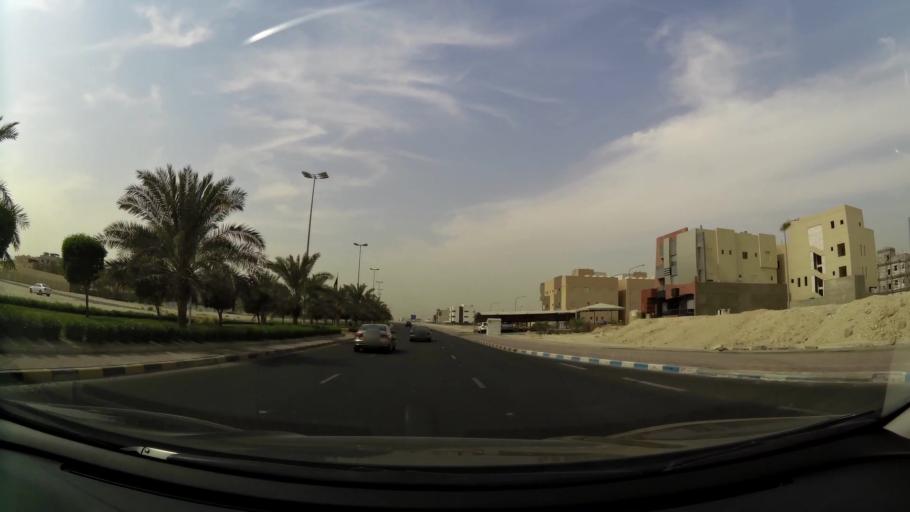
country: KW
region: Al Farwaniyah
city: Janub as Surrah
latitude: 29.2857
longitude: 47.9996
